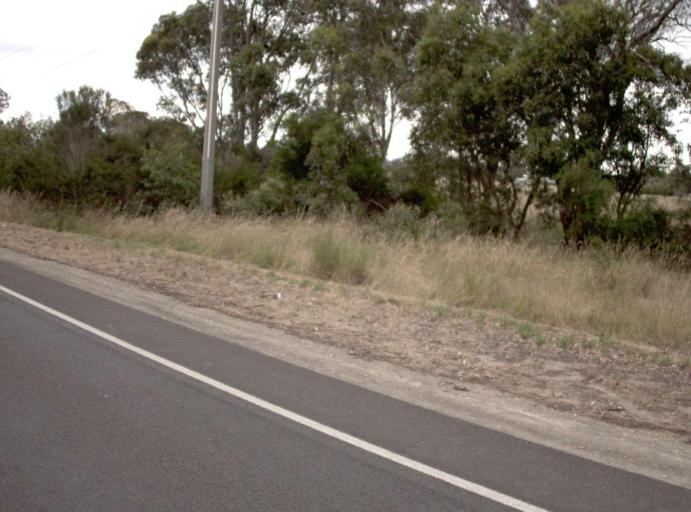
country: AU
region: Victoria
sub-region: Wellington
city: Sale
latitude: -38.1669
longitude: 147.0870
